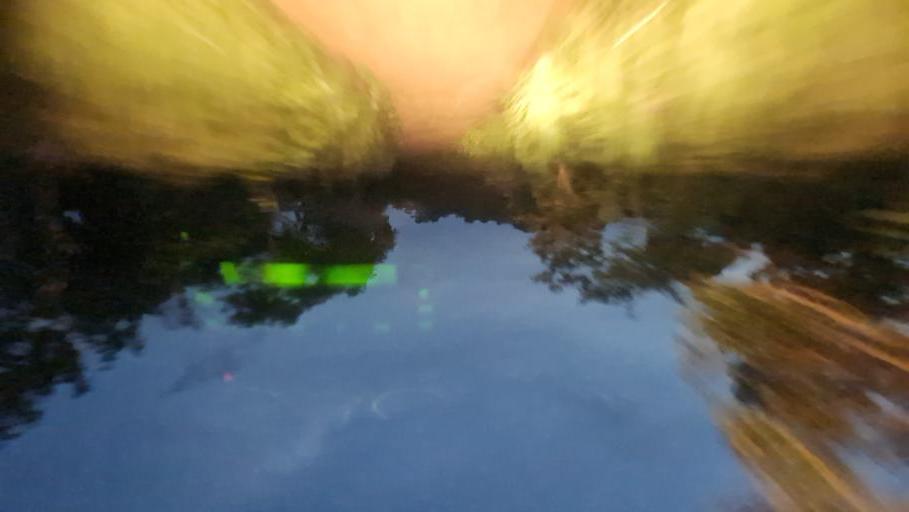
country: MZ
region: Nampula
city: Nampula
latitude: -14.6770
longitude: 39.8312
